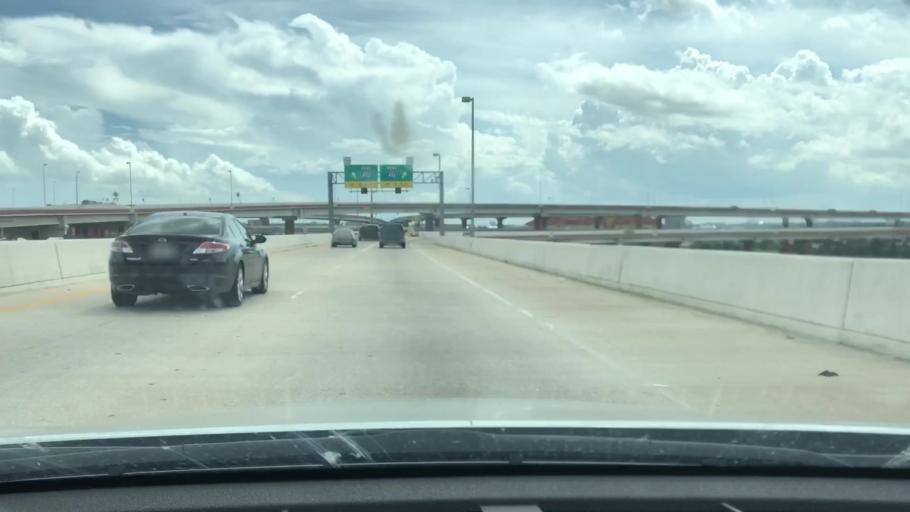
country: US
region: Texas
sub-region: Bexar County
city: Castle Hills
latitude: 29.5235
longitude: -98.4817
